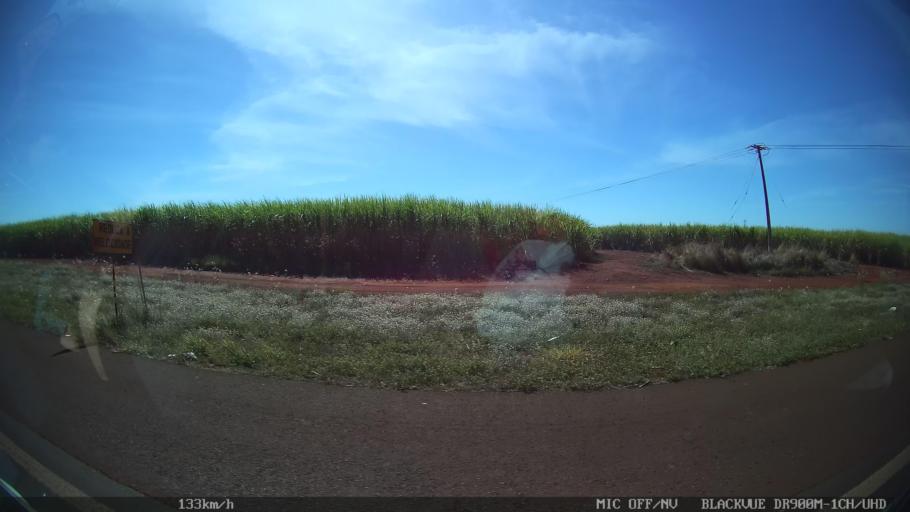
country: BR
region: Sao Paulo
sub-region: Guaira
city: Guaira
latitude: -20.4437
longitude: -48.3094
